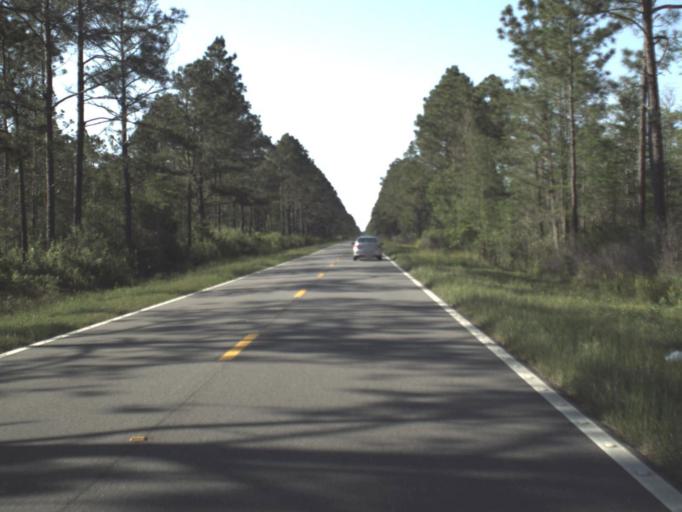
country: US
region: Florida
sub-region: Gulf County
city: Wewahitchka
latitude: 30.0896
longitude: -84.9841
